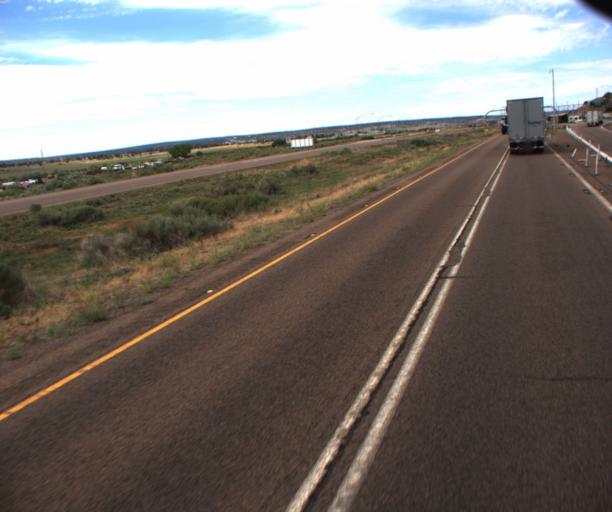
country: US
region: Arizona
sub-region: Apache County
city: Houck
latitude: 35.2260
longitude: -109.3184
